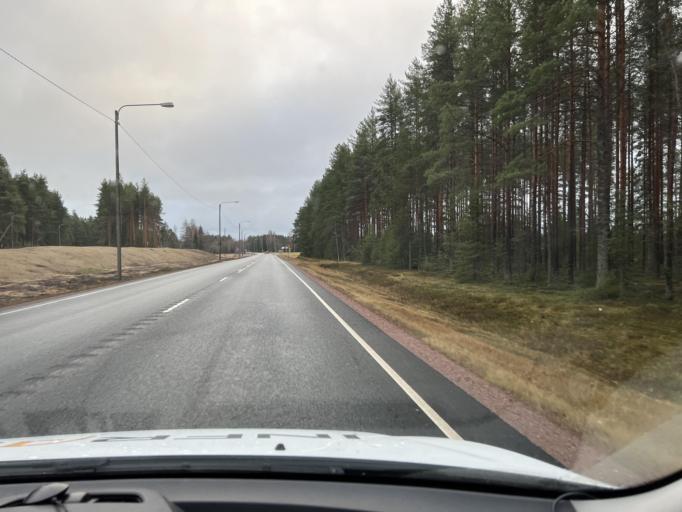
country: FI
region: Northern Ostrobothnia
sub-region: Oulu
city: Muhos
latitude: 64.8756
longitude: 25.8568
